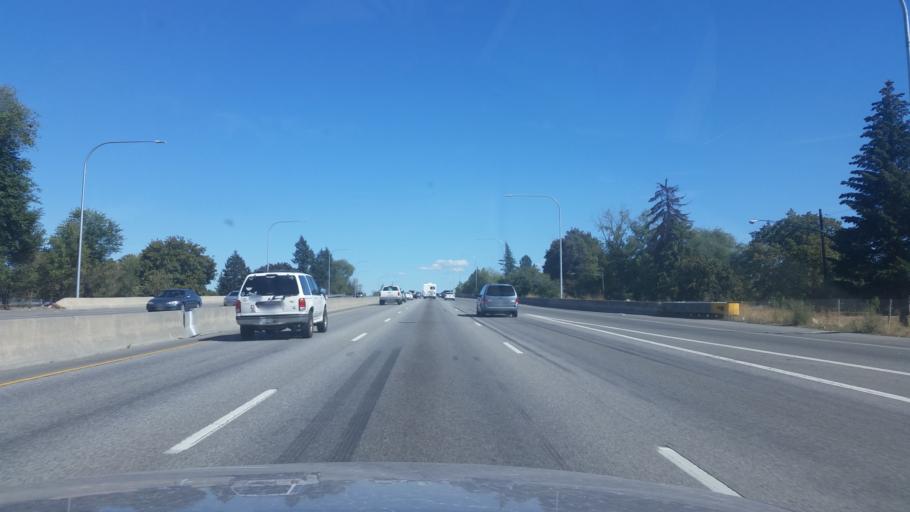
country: US
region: Washington
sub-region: Spokane County
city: Spokane
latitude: 47.6538
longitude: -117.3548
